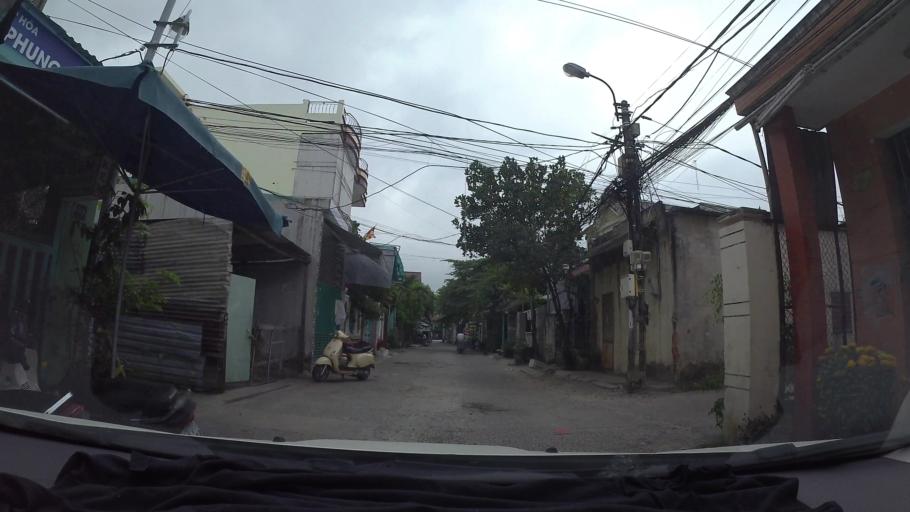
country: VN
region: Da Nang
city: Lien Chieu
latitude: 16.0705
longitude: 108.1521
